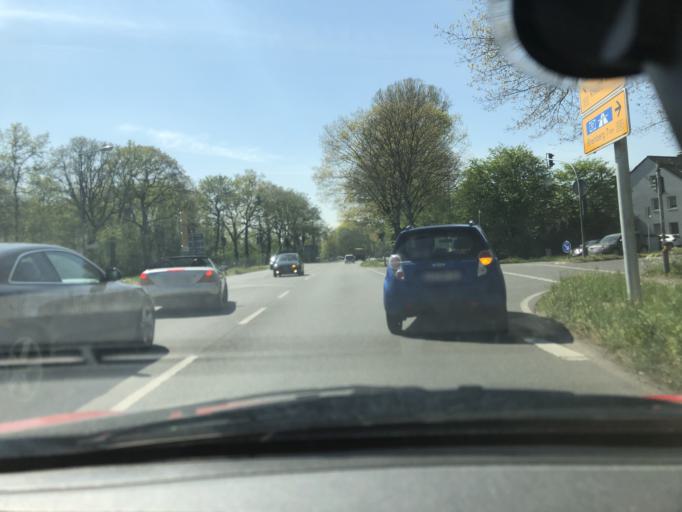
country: DE
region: North Rhine-Westphalia
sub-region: Regierungsbezirk Dusseldorf
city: Kamp-Lintfort
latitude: 51.5048
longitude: 6.5232
